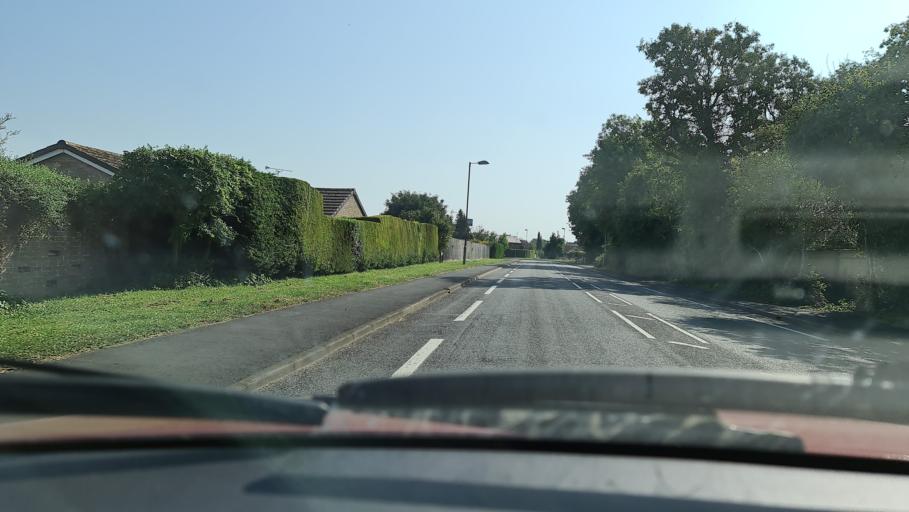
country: GB
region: England
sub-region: Oxfordshire
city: Bicester
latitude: 51.9081
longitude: -1.1670
